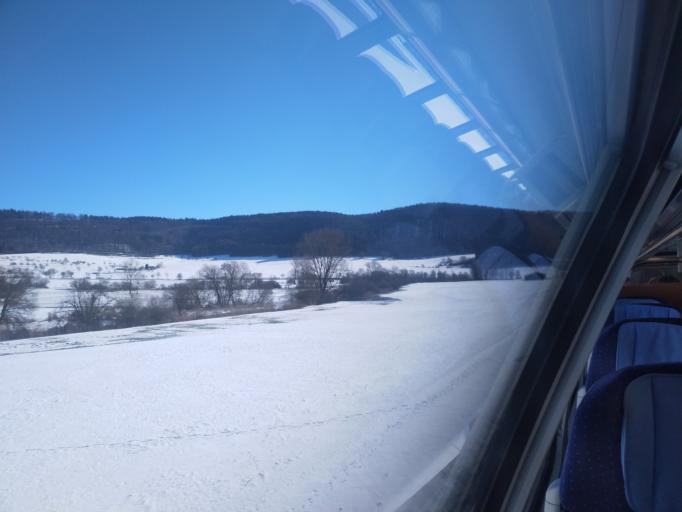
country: DE
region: Baden-Wuerttemberg
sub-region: Freiburg Region
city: Durbheim
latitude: 48.0501
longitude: 8.7781
